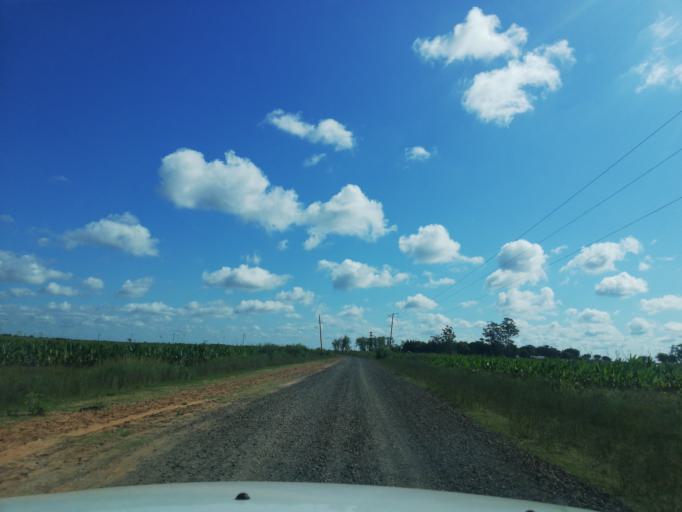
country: AR
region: Corrientes
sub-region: Departamento de San Miguel
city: San Miguel
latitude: -27.9838
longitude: -57.5823
